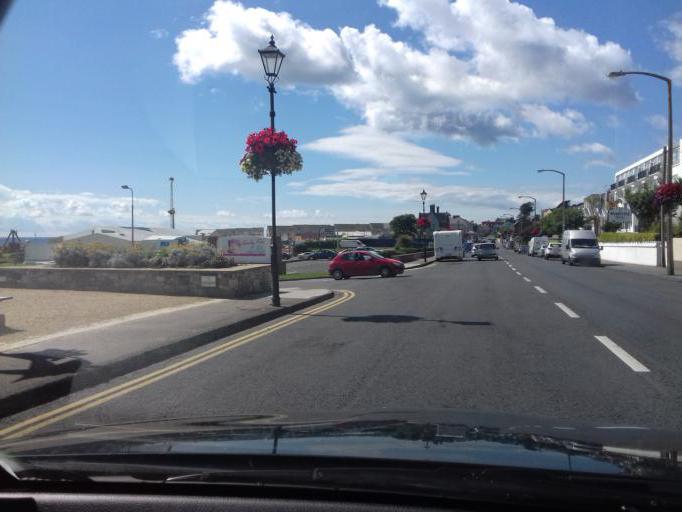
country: IE
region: Munster
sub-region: Waterford
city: Tra Mhor
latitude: 52.1637
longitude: -7.1473
